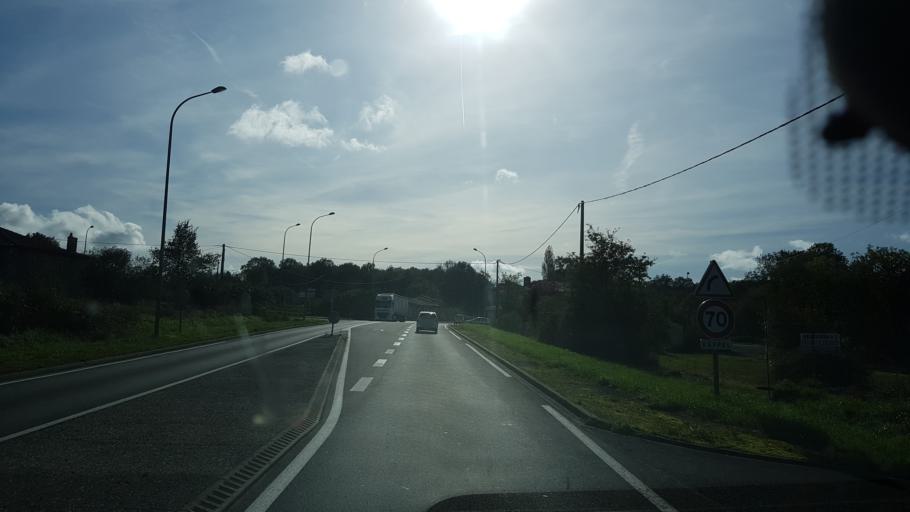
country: FR
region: Poitou-Charentes
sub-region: Departement de la Charente
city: Loubert
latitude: 45.9373
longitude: 0.5375
